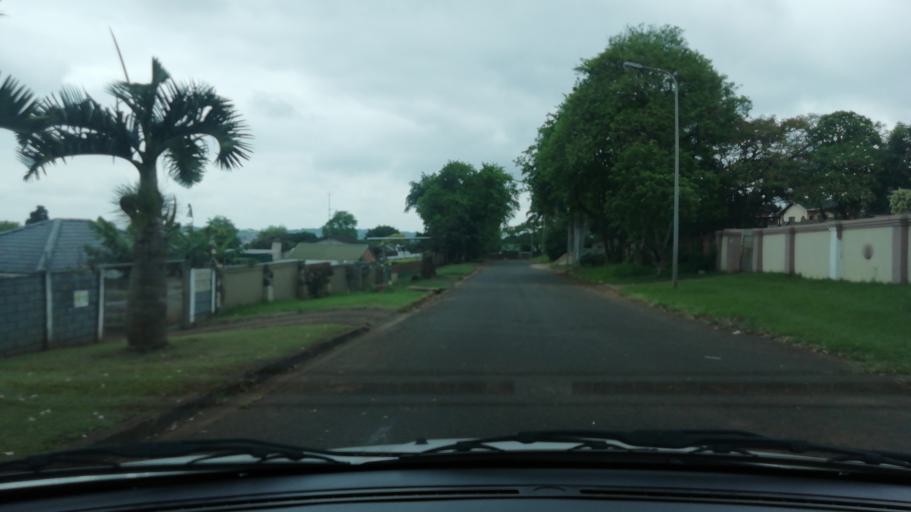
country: ZA
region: KwaZulu-Natal
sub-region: uThungulu District Municipality
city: Empangeni
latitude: -28.7670
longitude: 31.8929
